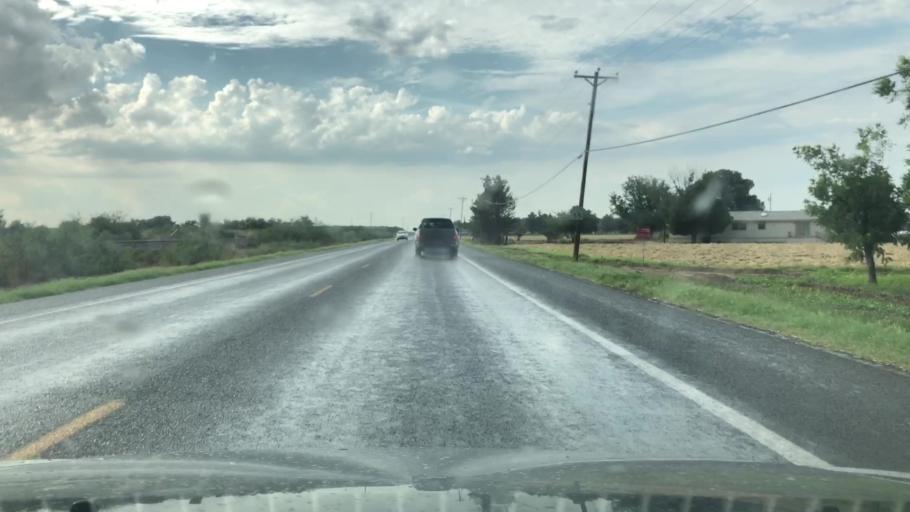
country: US
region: New Mexico
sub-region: Dona Ana County
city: Mesquite
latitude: 32.2049
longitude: -106.7220
